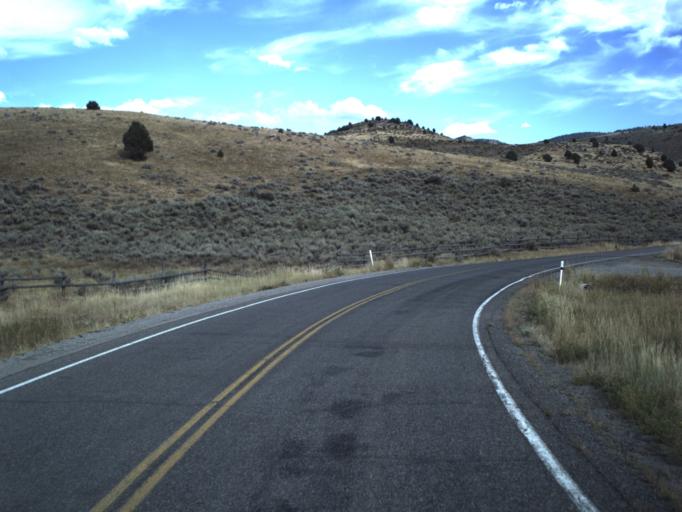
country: US
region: Utah
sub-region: Cache County
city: Millville
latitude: 41.6063
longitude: -111.5807
